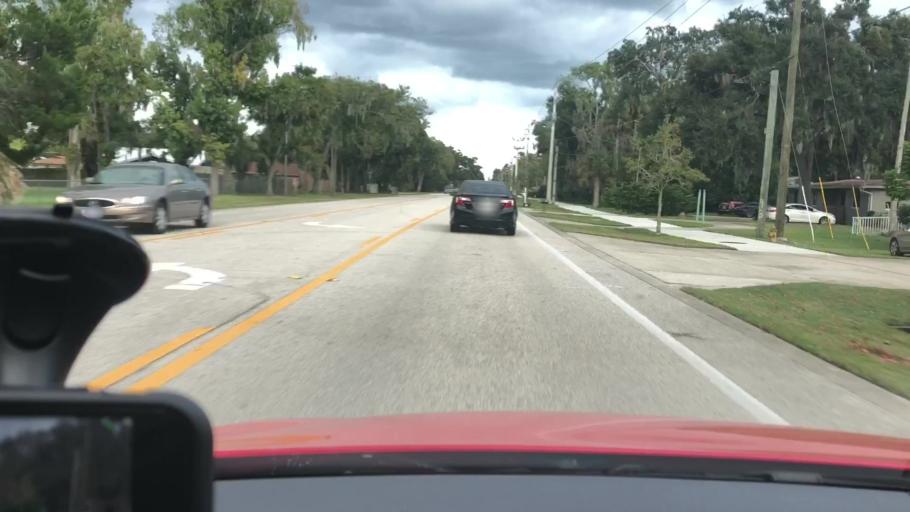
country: US
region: Florida
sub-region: Volusia County
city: South Daytona
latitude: 29.1687
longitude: -81.0174
